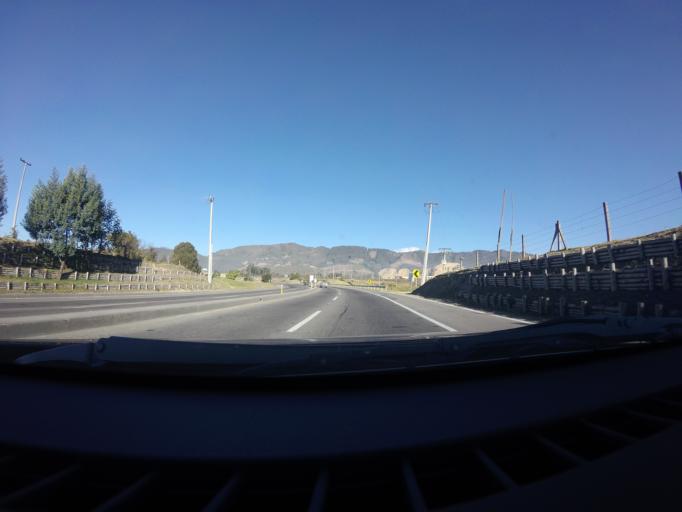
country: CO
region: Cundinamarca
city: Cajica
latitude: 4.9362
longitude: -74.0132
